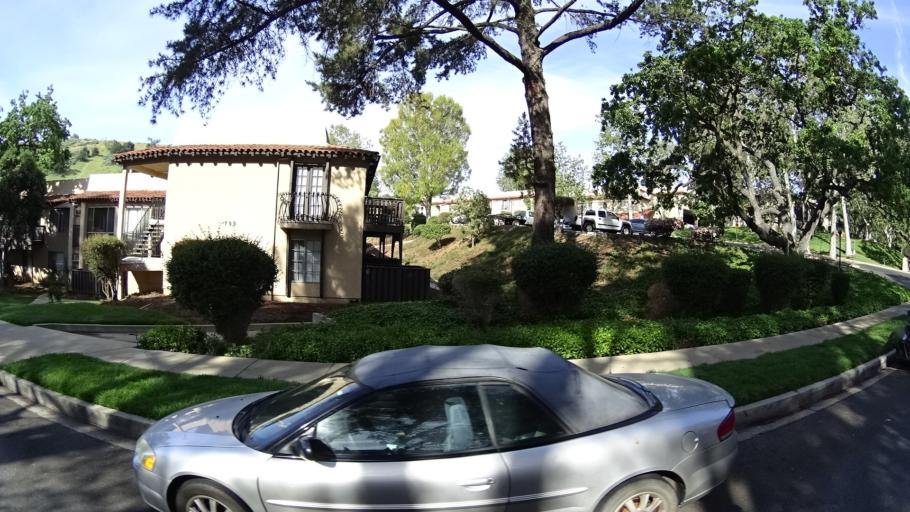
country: US
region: California
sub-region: Ventura County
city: Thousand Oaks
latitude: 34.1885
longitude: -118.8795
